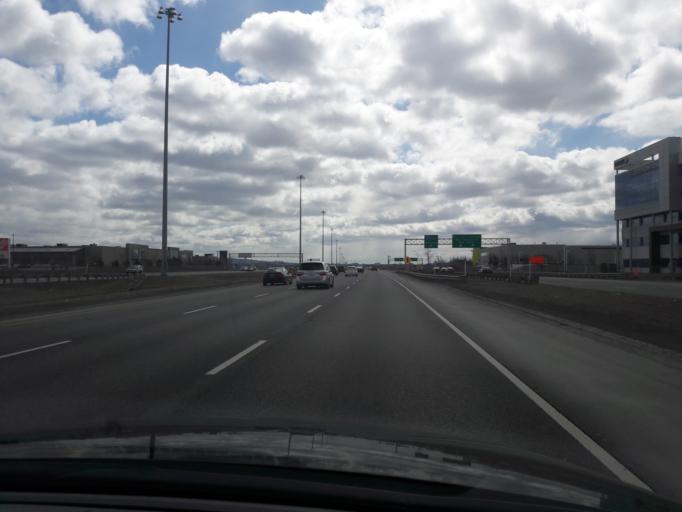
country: CA
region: Quebec
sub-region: Laval
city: Laval
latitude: 45.5571
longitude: -73.7314
